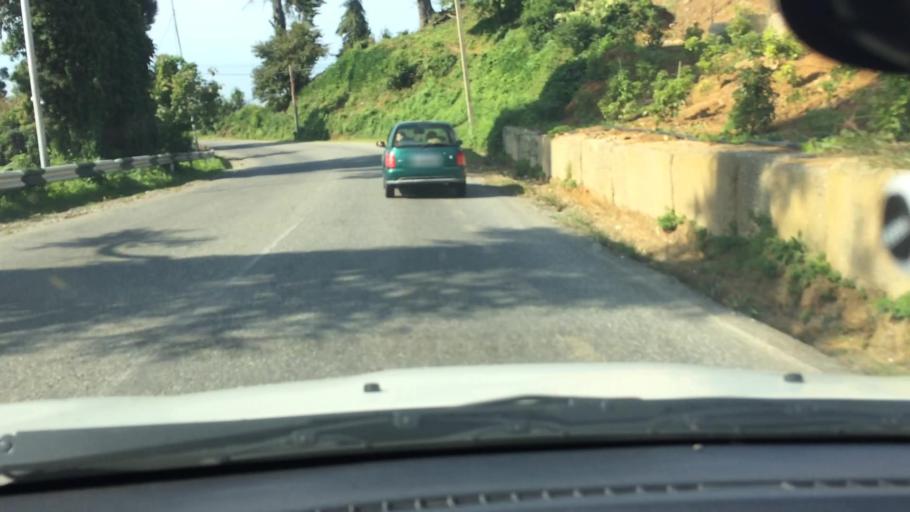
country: GE
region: Ajaria
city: Kobuleti
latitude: 41.7503
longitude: 41.7437
